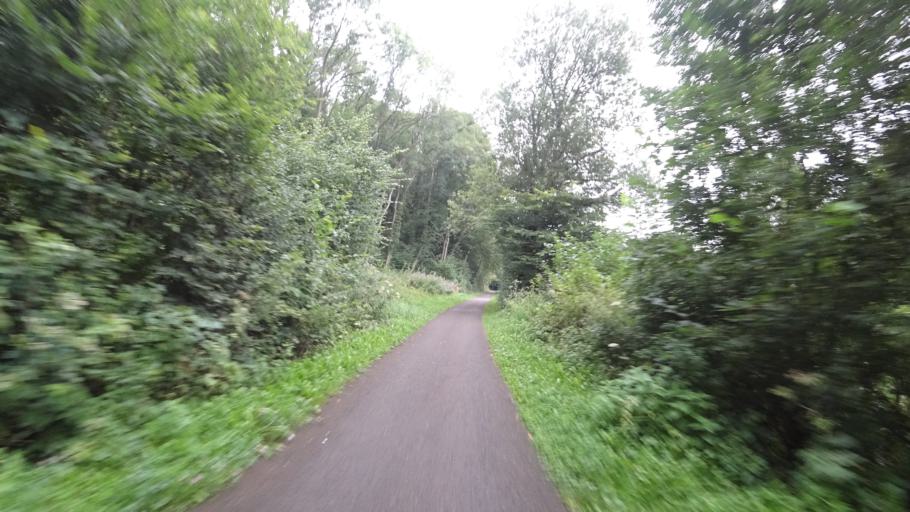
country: BE
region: Wallonia
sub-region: Province de Namur
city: Namur
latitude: 50.4969
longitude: 4.8653
